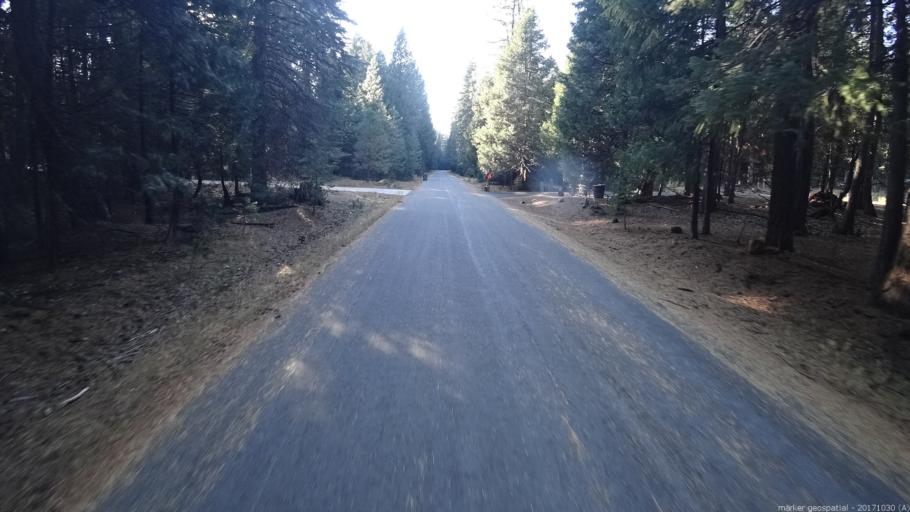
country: US
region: California
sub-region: Shasta County
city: Shingletown
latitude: 40.5520
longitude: -121.7204
